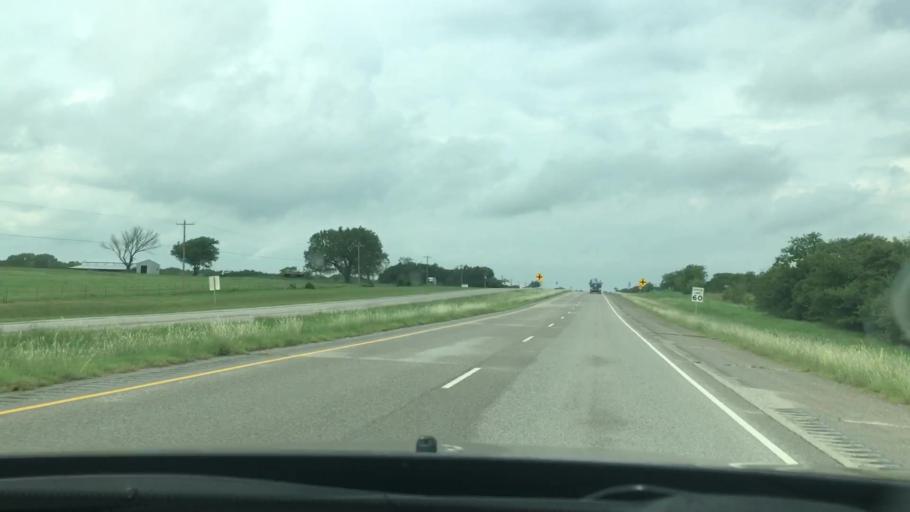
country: US
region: Oklahoma
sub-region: Carter County
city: Wilson
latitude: 34.1731
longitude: -97.4680
